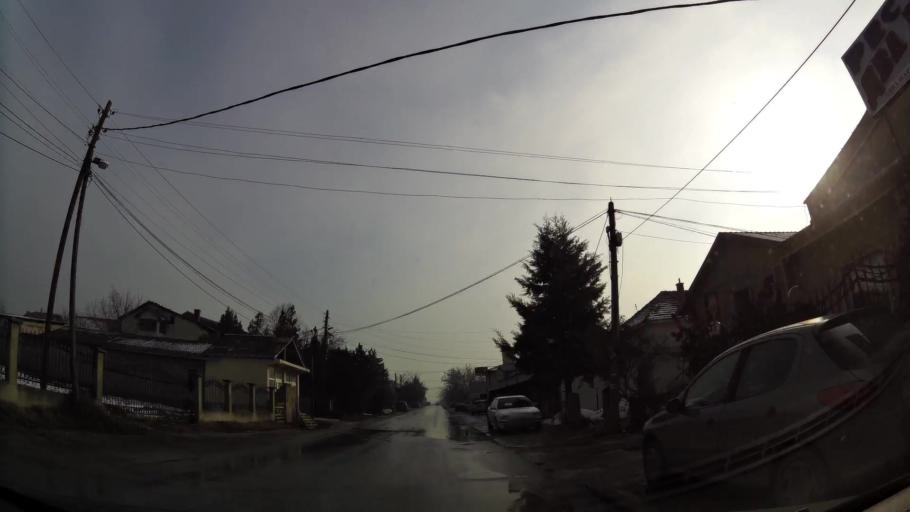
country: MK
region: Ilinden
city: Marino
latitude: 41.9929
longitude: 21.5891
